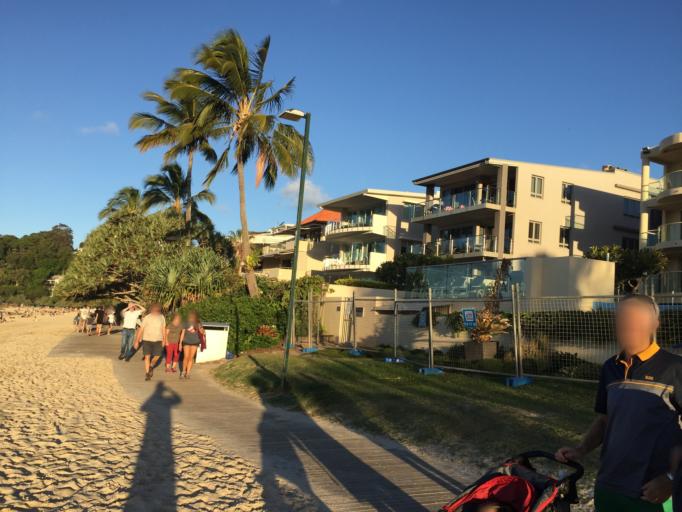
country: AU
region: Queensland
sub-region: Sunshine Coast
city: Noosa Heads
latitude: -26.3857
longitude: 153.0890
